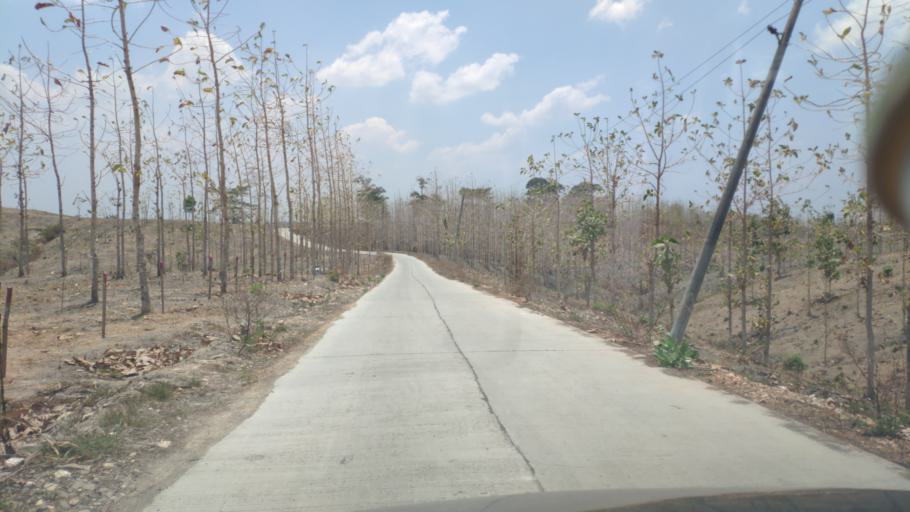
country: ID
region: Central Java
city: Temulus
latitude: -7.2858
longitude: 111.3750
